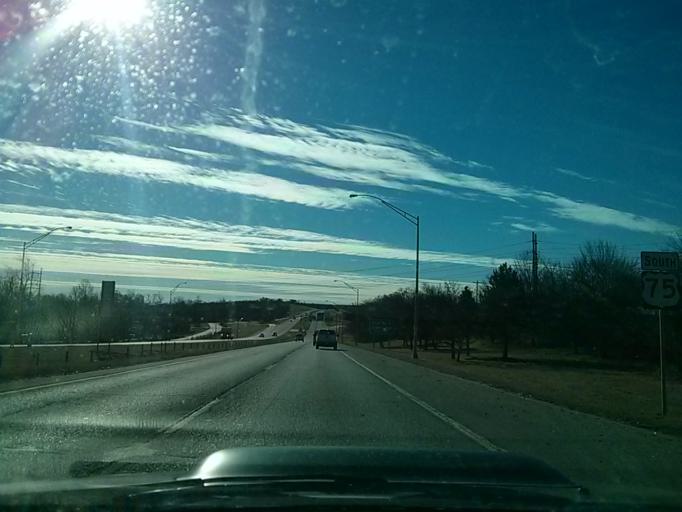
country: US
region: Oklahoma
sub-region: Tulsa County
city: Tulsa
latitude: 36.1101
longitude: -96.0119
